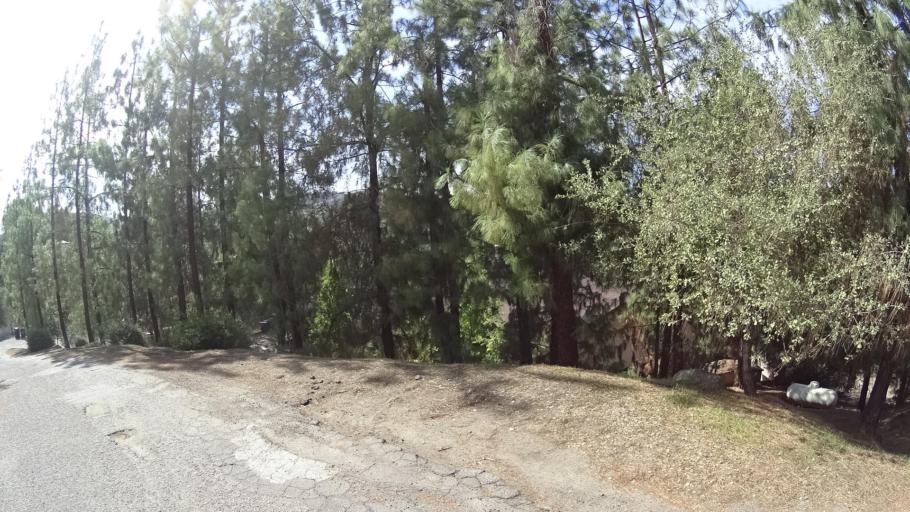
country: US
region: California
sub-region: San Diego County
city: Alpine
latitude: 32.8373
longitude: -116.7970
